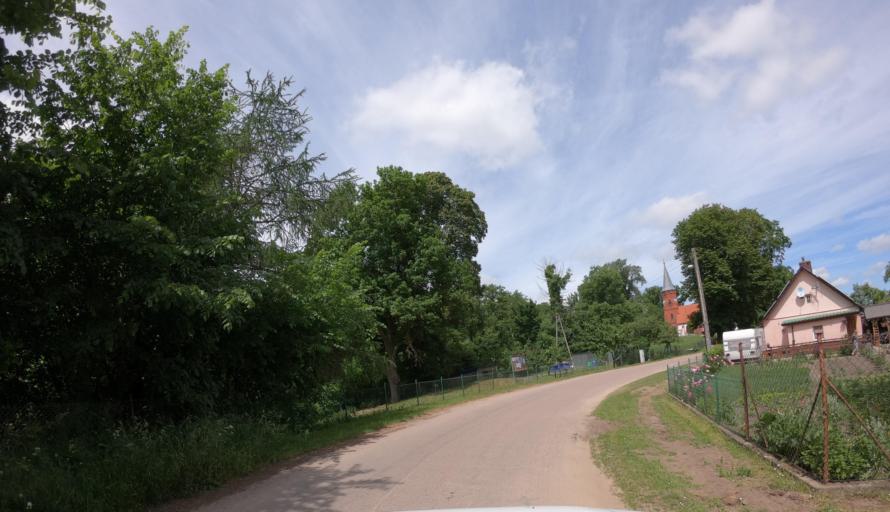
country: PL
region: West Pomeranian Voivodeship
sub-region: Powiat kamienski
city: Wolin
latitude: 53.8246
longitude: 14.7087
